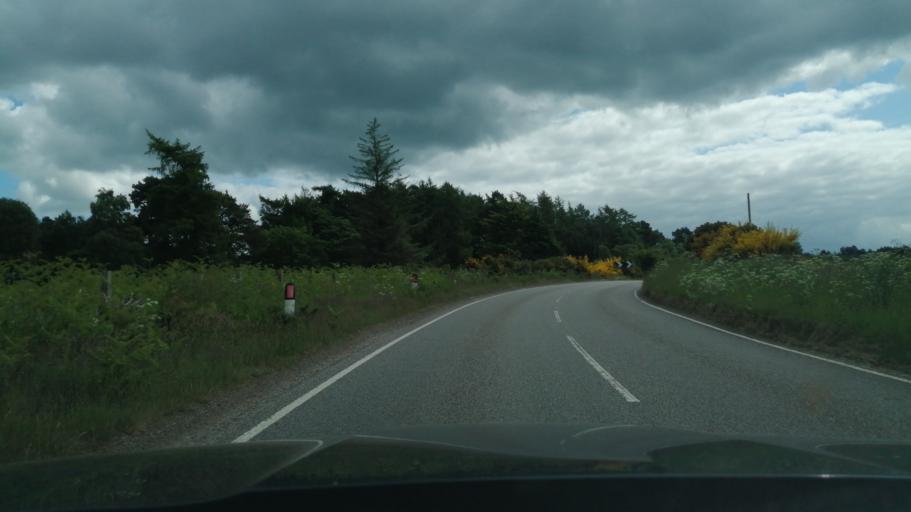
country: GB
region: Scotland
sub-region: Moray
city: Lhanbryd
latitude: 57.6208
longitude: -3.2125
